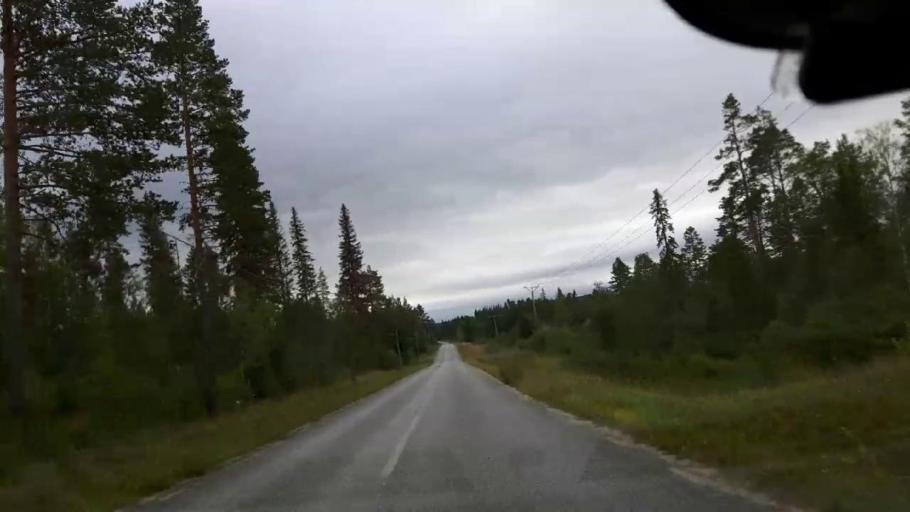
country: SE
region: Jaemtland
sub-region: Braecke Kommun
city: Braecke
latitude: 62.8845
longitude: 15.6190
